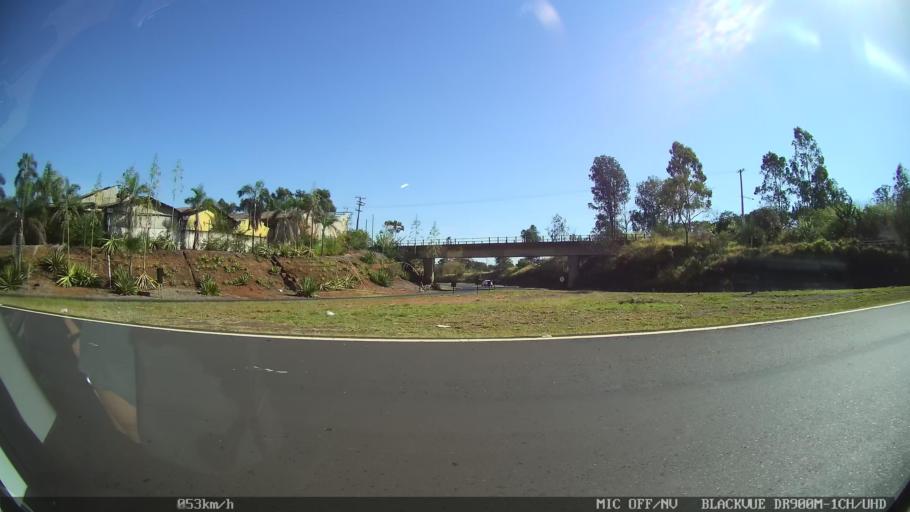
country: BR
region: Sao Paulo
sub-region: Batatais
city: Batatais
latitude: -20.9004
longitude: -47.6073
